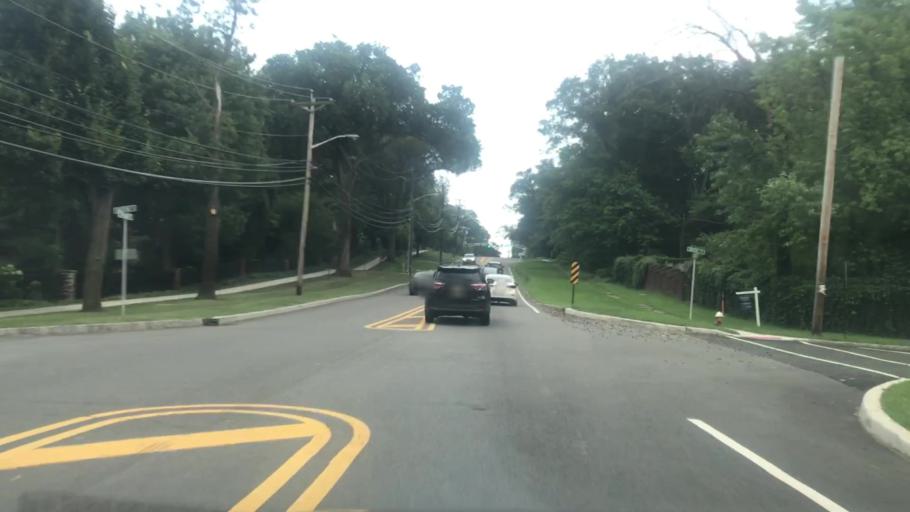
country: US
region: New Jersey
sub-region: Bergen County
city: Englewood
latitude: 40.8880
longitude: -73.9644
